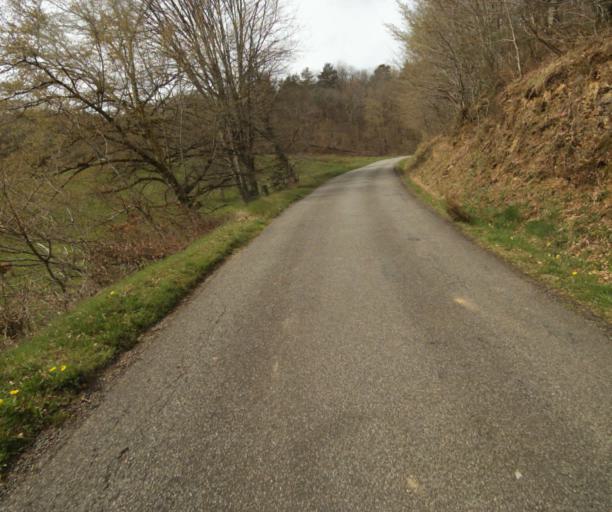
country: FR
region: Limousin
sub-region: Departement de la Correze
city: Laguenne
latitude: 45.2424
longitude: 1.8433
